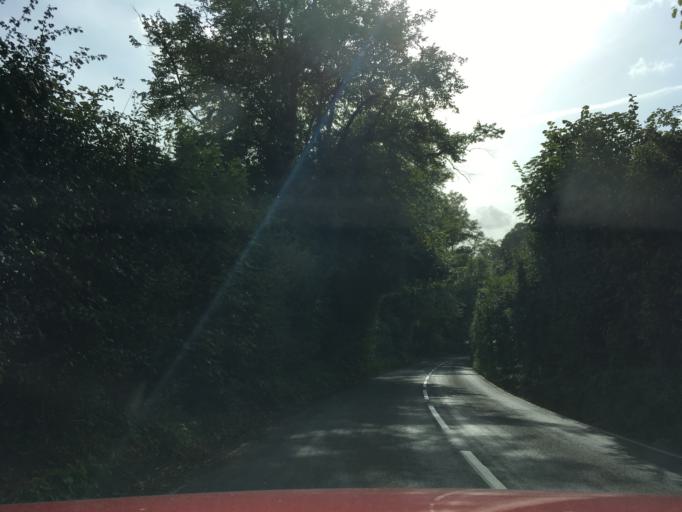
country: GB
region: England
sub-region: Gloucestershire
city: Wotton-under-Edge
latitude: 51.6440
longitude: -2.3411
